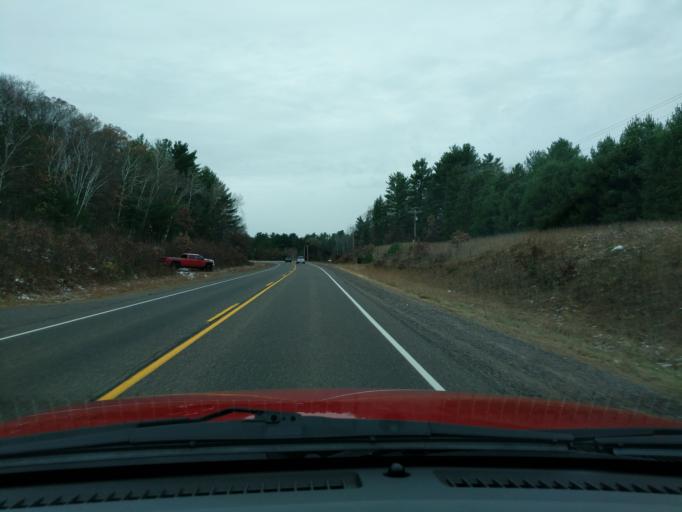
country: US
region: Wisconsin
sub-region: Burnett County
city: Siren
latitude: 45.8273
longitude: -92.2980
